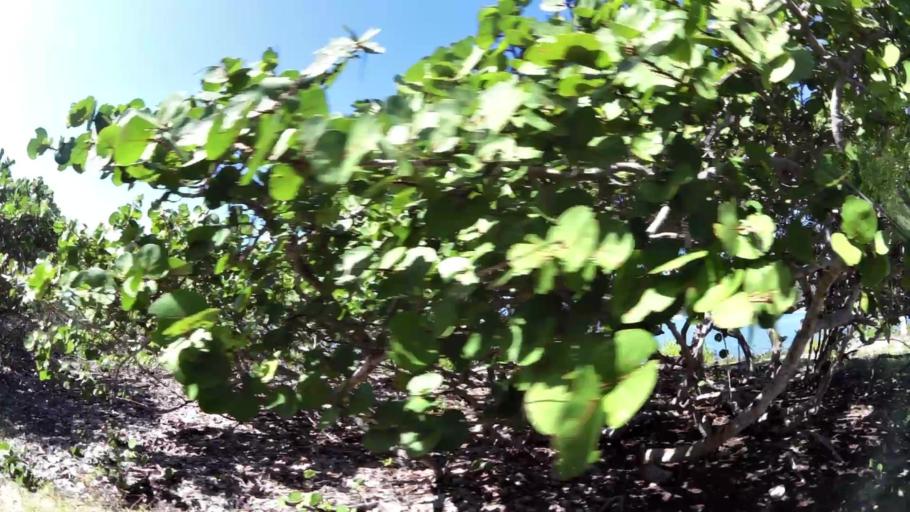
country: VG
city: Tortola
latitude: 18.4461
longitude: -64.5291
